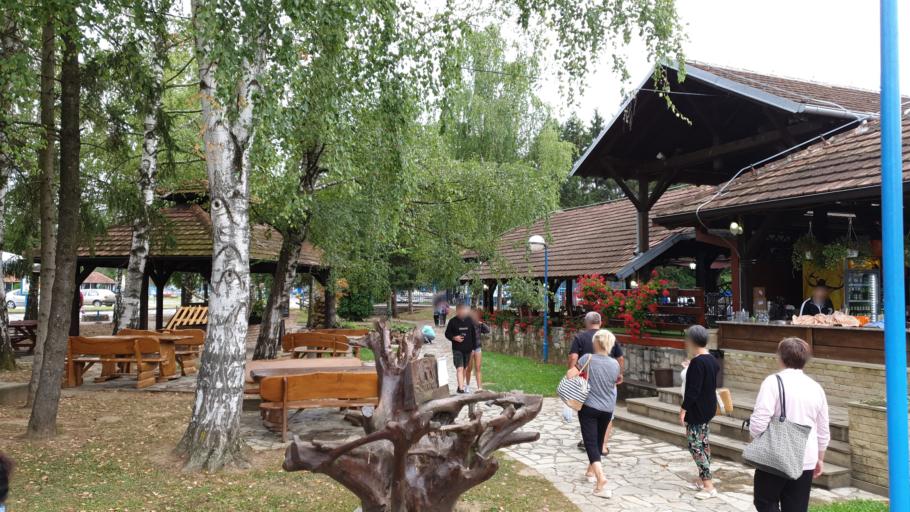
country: RS
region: Central Serbia
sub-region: Kolubarski Okrug
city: Mionica
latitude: 44.2218
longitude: 20.1551
